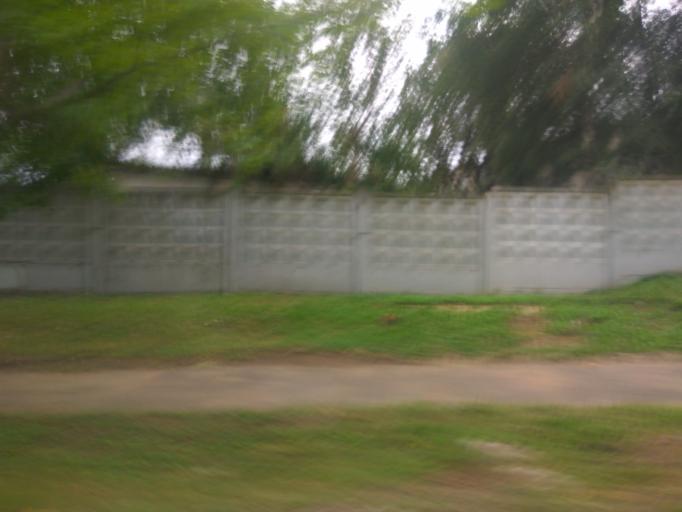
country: RU
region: Moskovskaya
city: Lyubertsy
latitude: 55.7009
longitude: 37.8813
